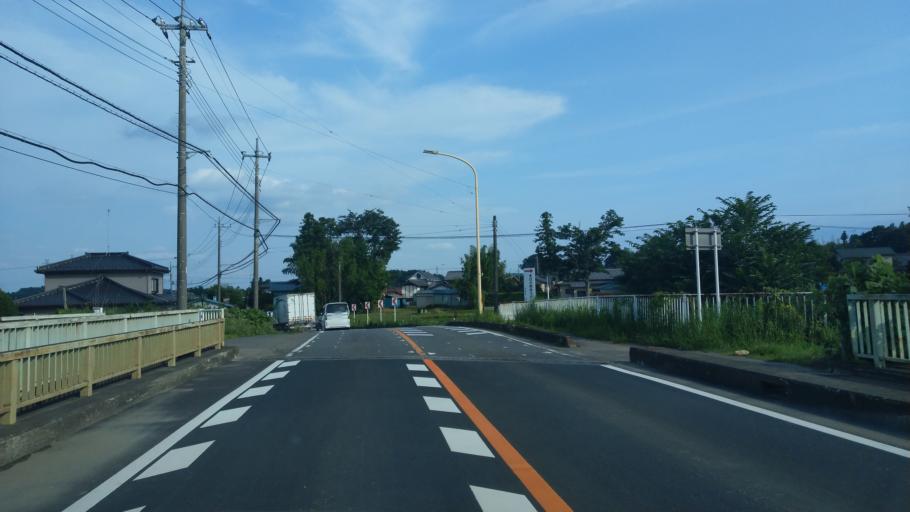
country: JP
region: Saitama
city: Ogawa
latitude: 36.0943
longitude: 139.2754
